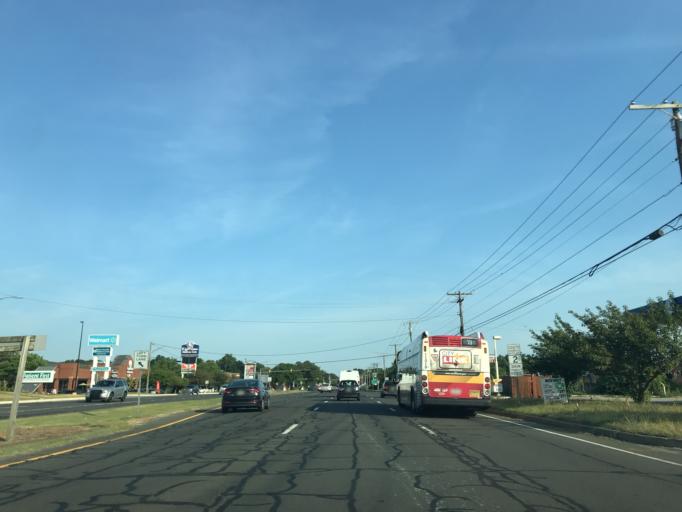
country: US
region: Maryland
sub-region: Anne Arundel County
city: Pasadena
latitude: 39.1256
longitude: -76.5894
